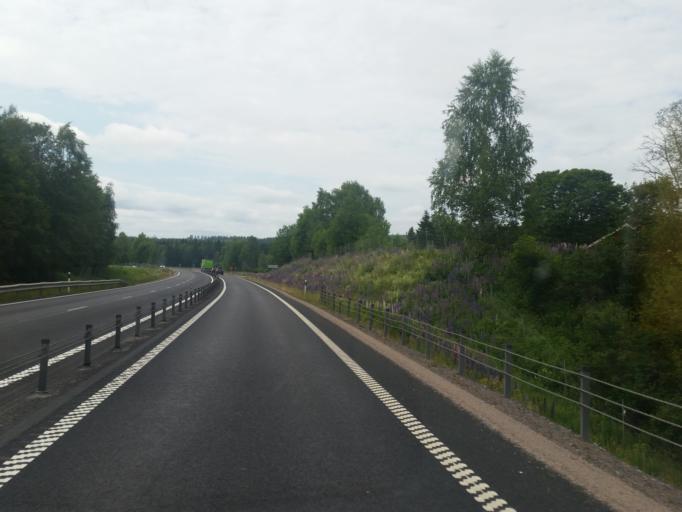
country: SE
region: Dalarna
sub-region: Borlange Kommun
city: Borlaenge
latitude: 60.4624
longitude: 15.3838
